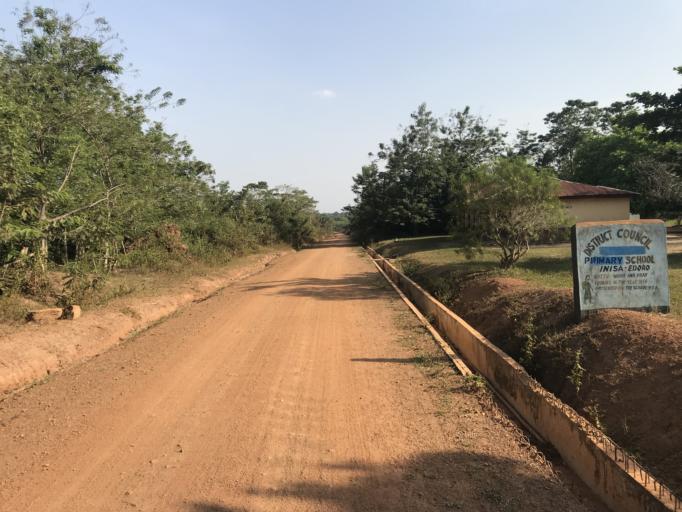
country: NG
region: Osun
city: Inisa
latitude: 7.8024
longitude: 4.2833
